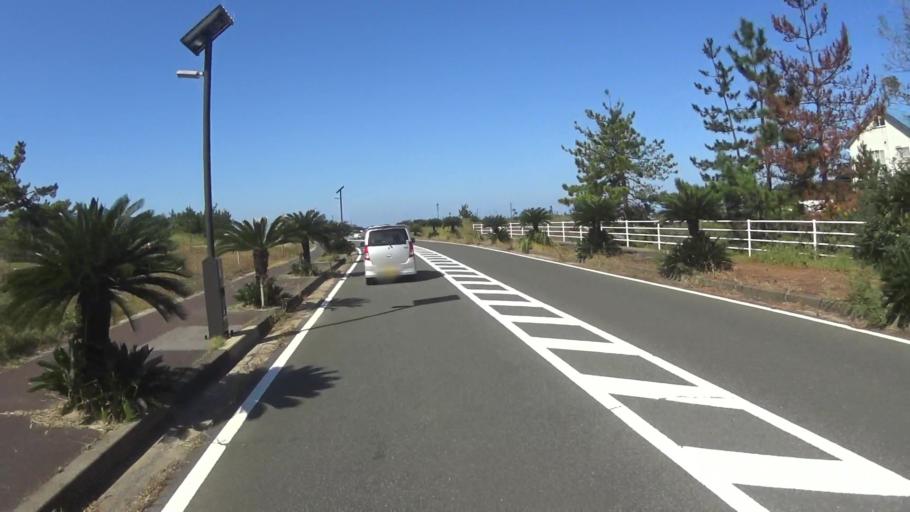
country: JP
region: Kyoto
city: Miyazu
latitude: 35.6902
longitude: 135.0315
